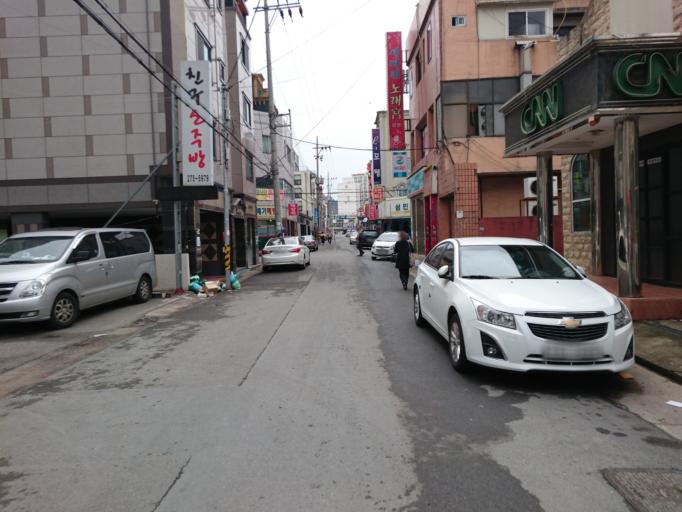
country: KR
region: Gyeongsangbuk-do
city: Enjitsu
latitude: 36.0146
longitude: 129.3474
